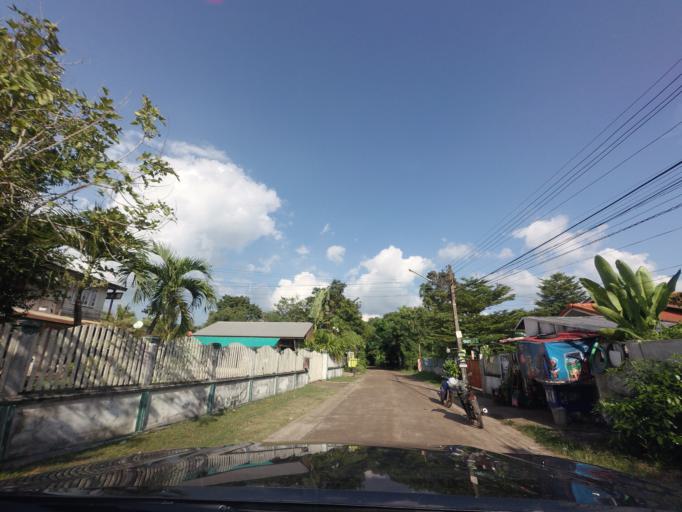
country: TH
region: Nong Khai
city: Nong Khai
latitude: 17.8859
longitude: 102.7711
